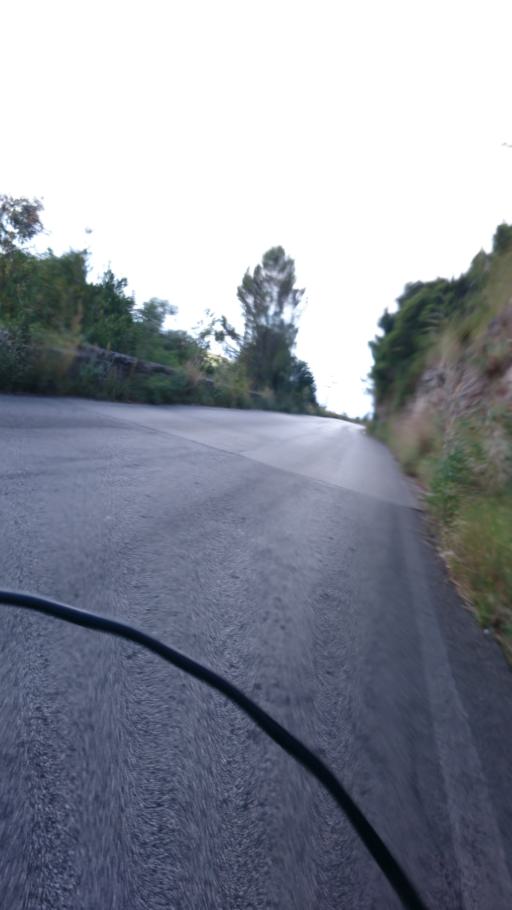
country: IT
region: Campania
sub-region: Provincia di Salerno
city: Camerota
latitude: 40.0250
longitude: 15.3726
